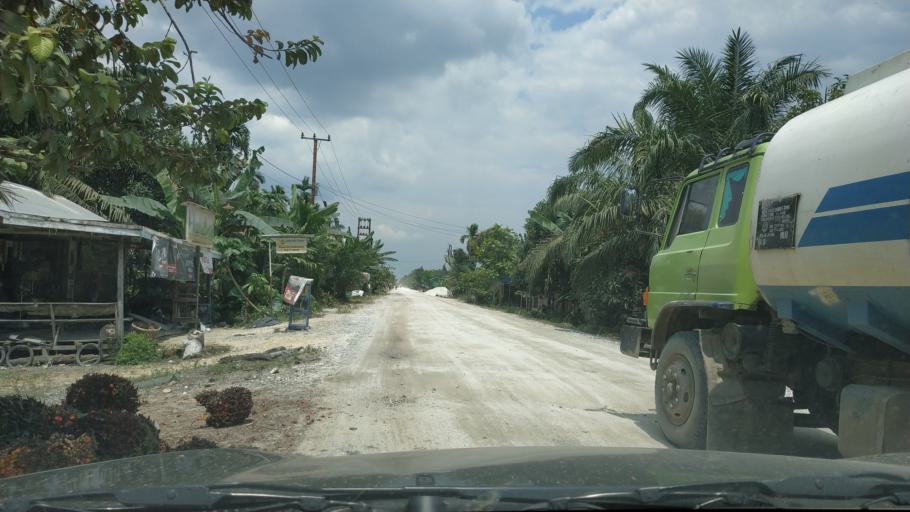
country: ID
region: Riau
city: Sungaisalak
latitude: -0.6002
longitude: 102.9003
